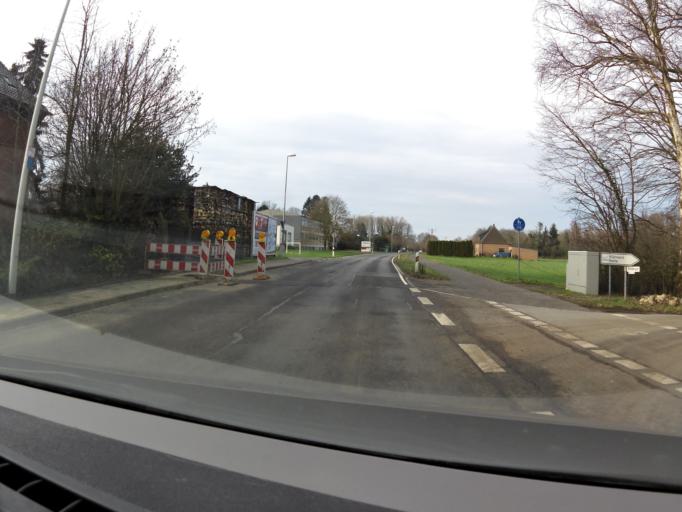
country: DE
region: North Rhine-Westphalia
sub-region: Regierungsbezirk Dusseldorf
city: Nettetal
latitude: 51.3065
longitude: 6.2453
